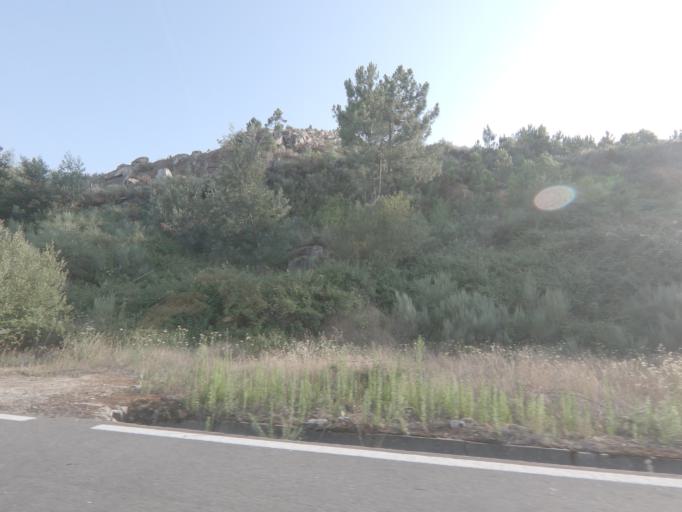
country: PT
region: Viseu
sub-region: Tabuaco
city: Tabuaco
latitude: 41.1177
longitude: -7.5799
